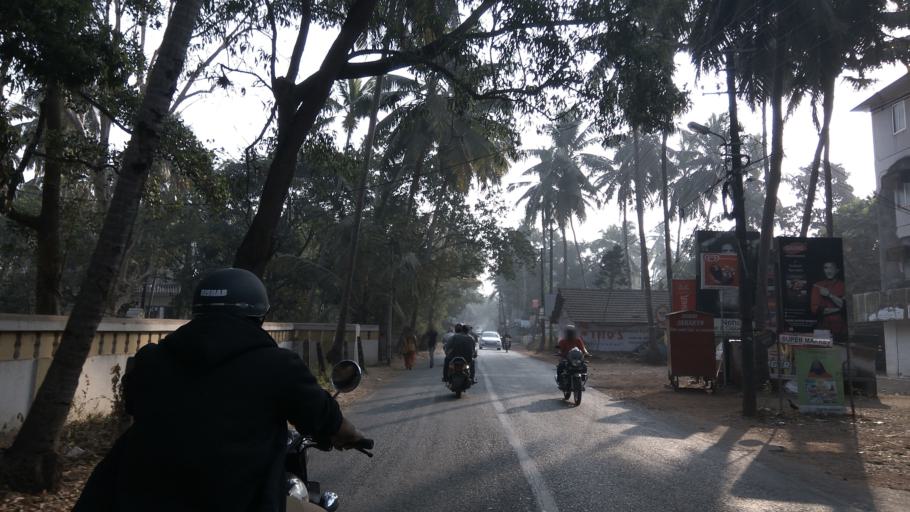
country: IN
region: Goa
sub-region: North Goa
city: Saligao
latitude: 15.5461
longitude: 73.7912
